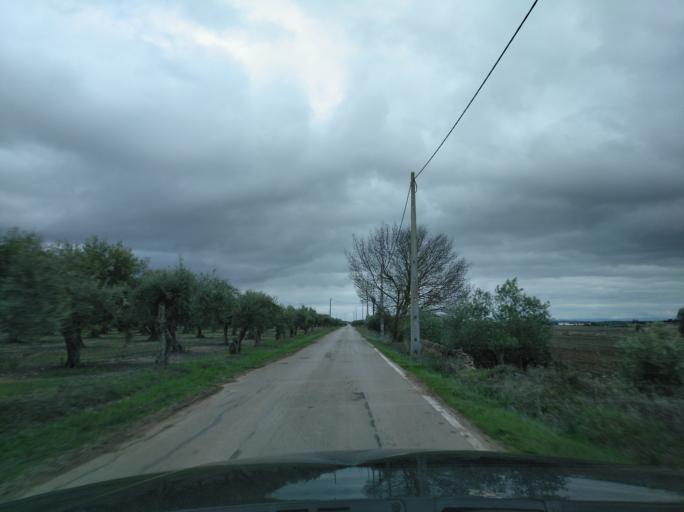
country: PT
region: Portalegre
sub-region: Campo Maior
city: Campo Maior
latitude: 38.9952
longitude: -7.0175
